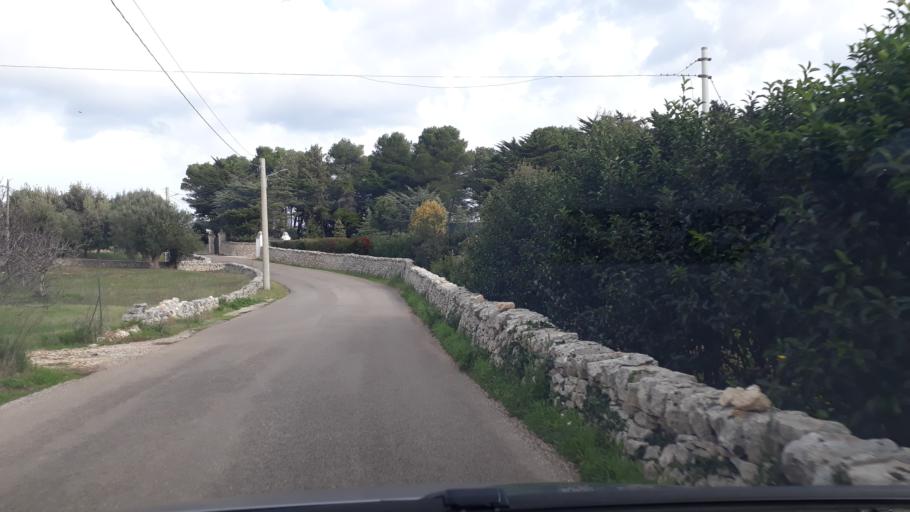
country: IT
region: Apulia
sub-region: Provincia di Brindisi
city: Cisternino
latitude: 40.7310
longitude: 17.4278
